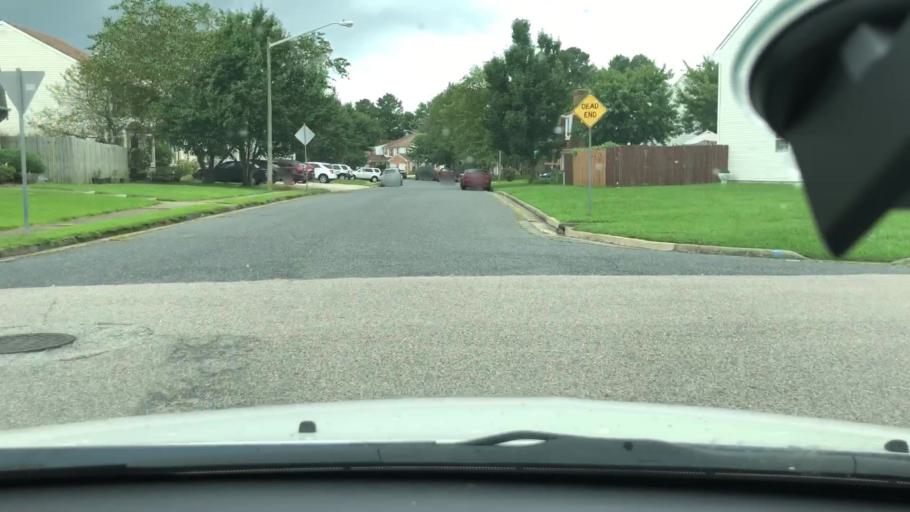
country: US
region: Virginia
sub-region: City of Virginia Beach
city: Virginia Beach
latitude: 36.8461
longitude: -76.1168
